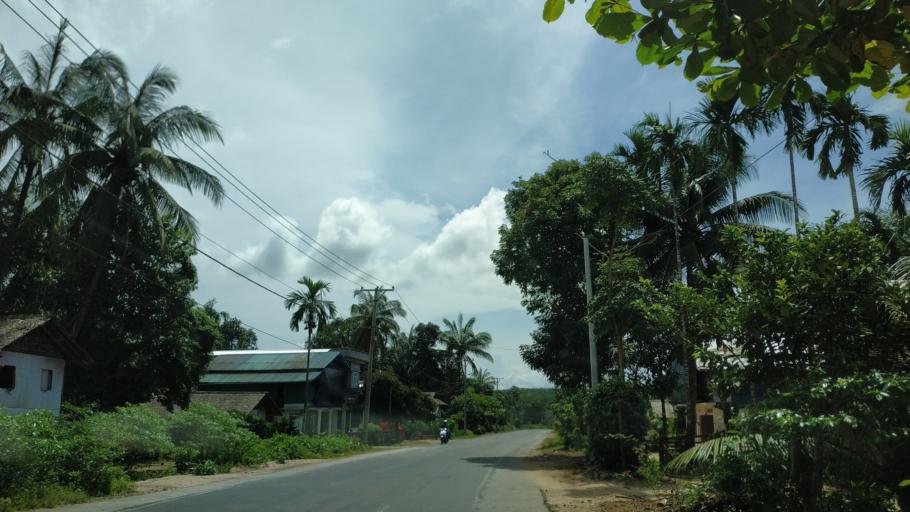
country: MM
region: Tanintharyi
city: Dawei
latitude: 14.1286
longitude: 98.1242
